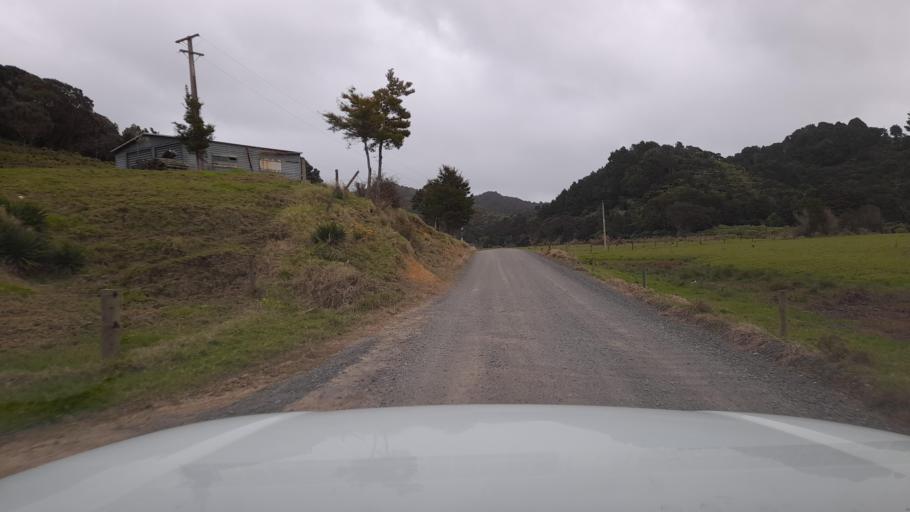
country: NZ
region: Northland
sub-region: Far North District
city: Paihia
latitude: -35.3455
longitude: 174.2286
